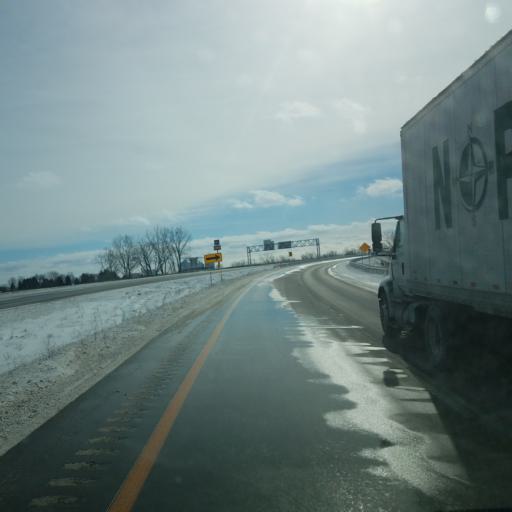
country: US
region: Michigan
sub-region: Gratiot County
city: Ithaca
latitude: 43.2944
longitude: -84.5828
